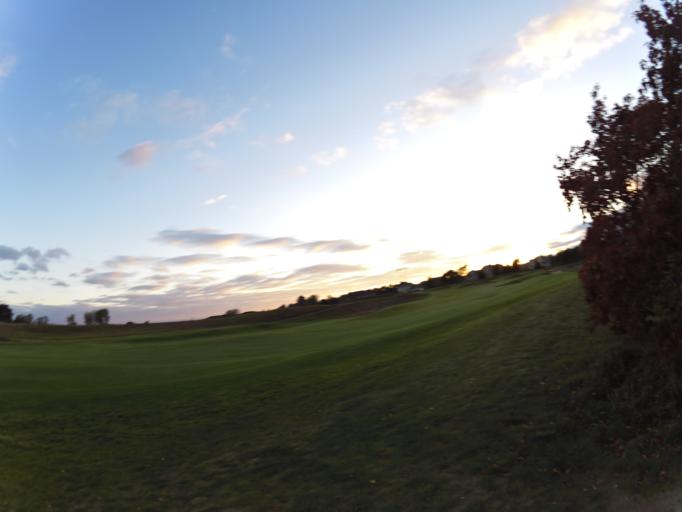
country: US
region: Minnesota
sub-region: Washington County
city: Lakeland
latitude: 44.9574
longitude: -92.8252
